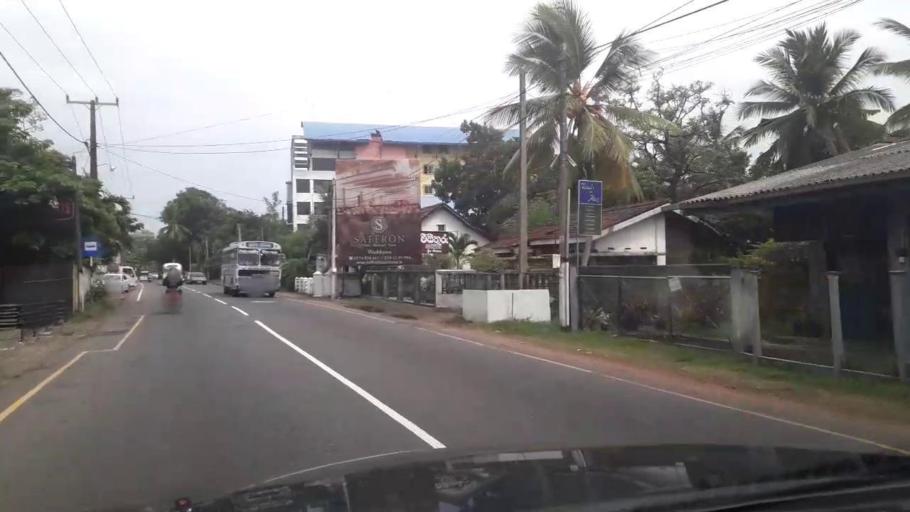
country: LK
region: Western
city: Panadura
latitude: 6.6816
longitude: 79.9213
